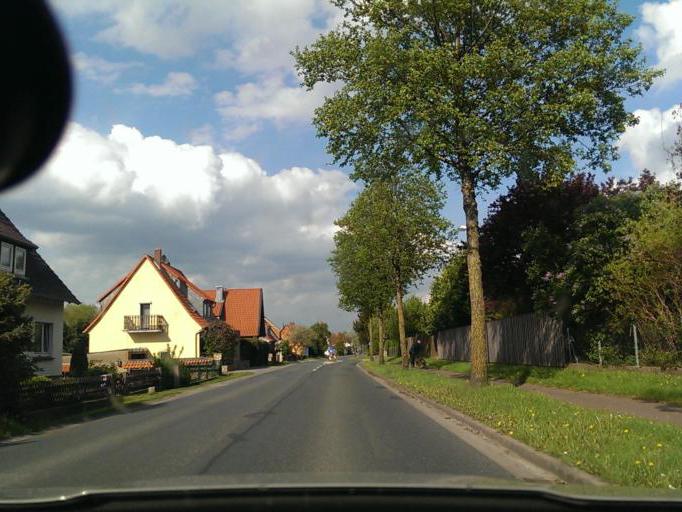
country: DE
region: Lower Saxony
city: Eime
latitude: 52.0704
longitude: 9.7125
